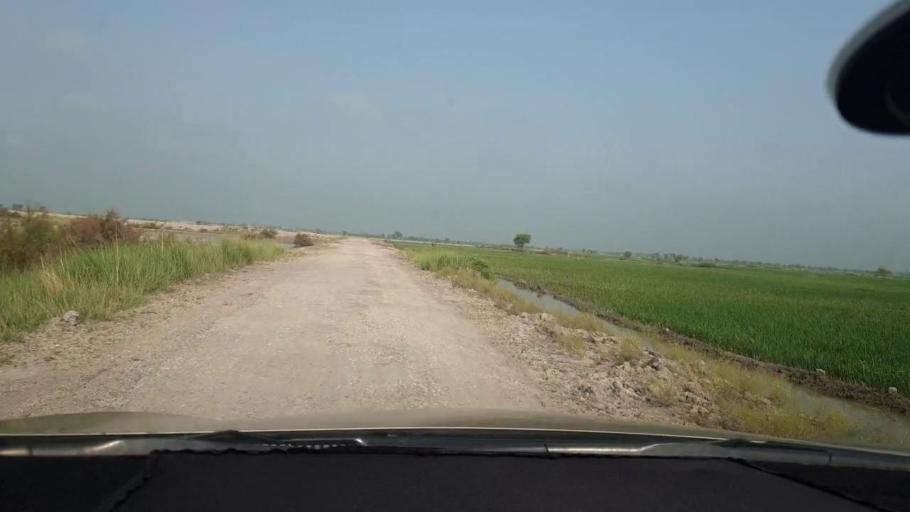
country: PK
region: Sindh
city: Kambar
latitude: 27.5344
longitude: 68.0640
